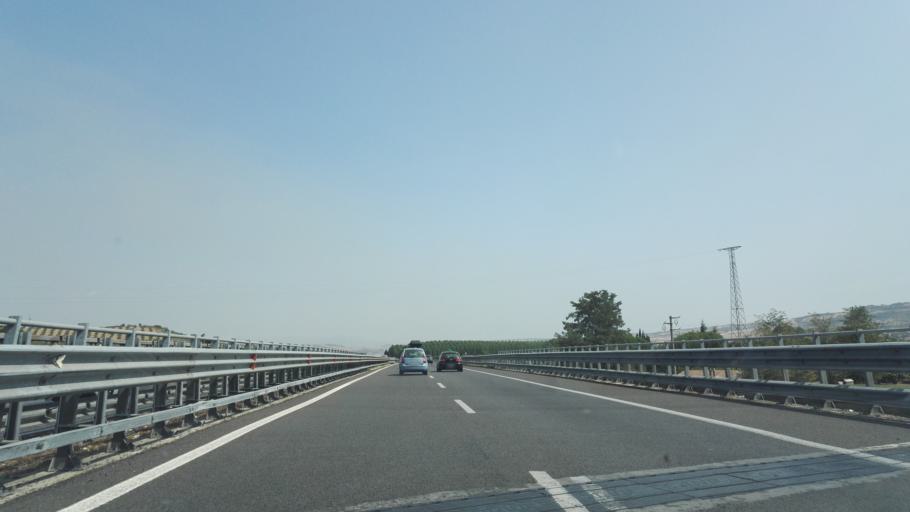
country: IT
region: Calabria
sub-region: Provincia di Cosenza
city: Sartano
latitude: 39.5326
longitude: 16.2210
